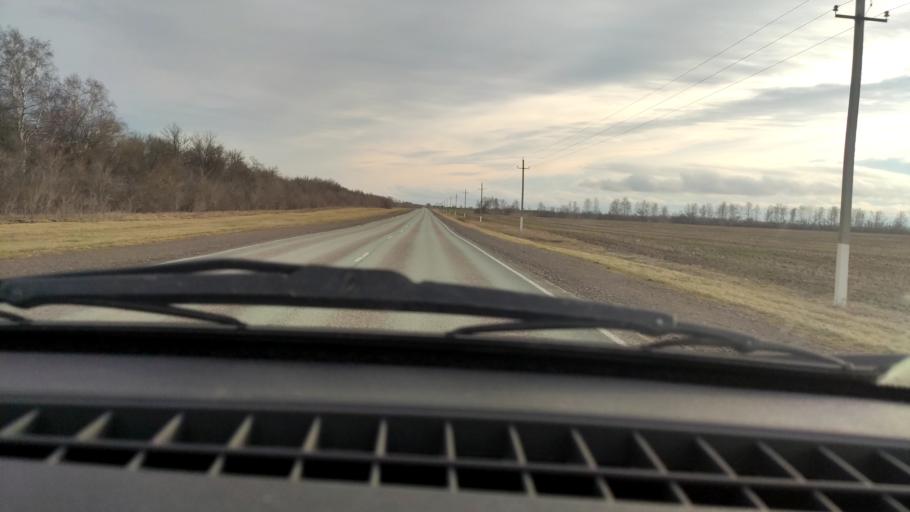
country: RU
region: Bashkortostan
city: Davlekanovo
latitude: 54.3134
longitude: 55.1469
